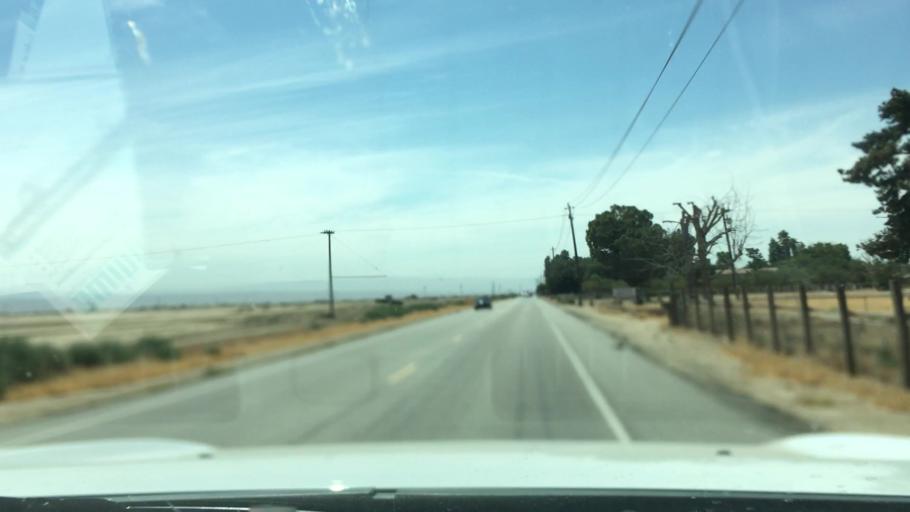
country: US
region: California
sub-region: Kern County
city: Rosedale
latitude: 35.3544
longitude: -119.2423
